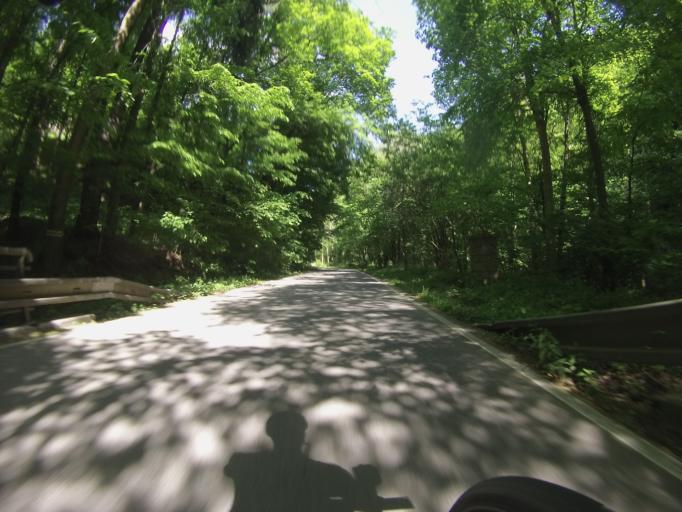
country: CZ
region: South Moravian
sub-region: Okres Blansko
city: Blansko
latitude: 49.3580
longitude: 16.6862
